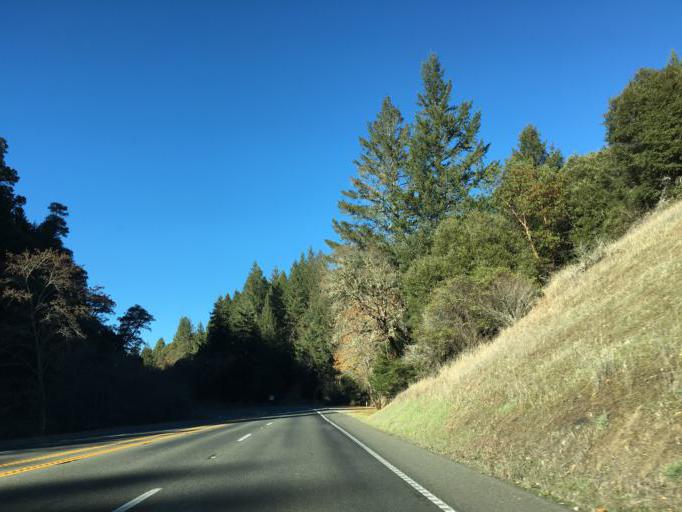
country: US
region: California
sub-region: Mendocino County
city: Laytonville
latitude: 39.5692
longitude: -123.4355
